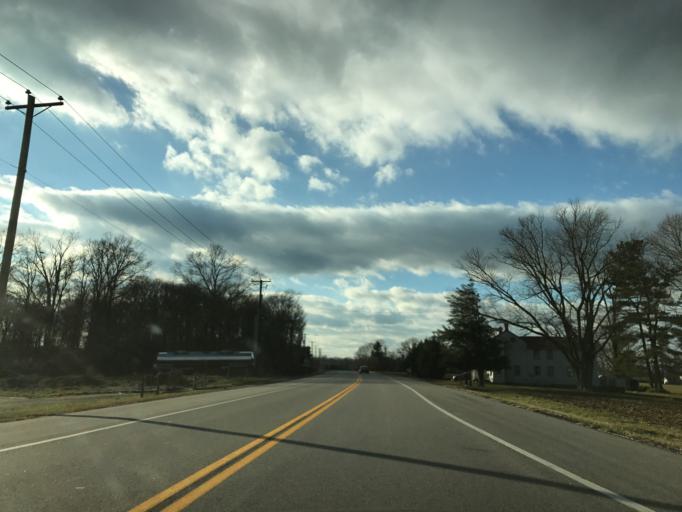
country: US
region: Maryland
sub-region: Cecil County
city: Rising Sun
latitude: 39.6620
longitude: -76.0058
